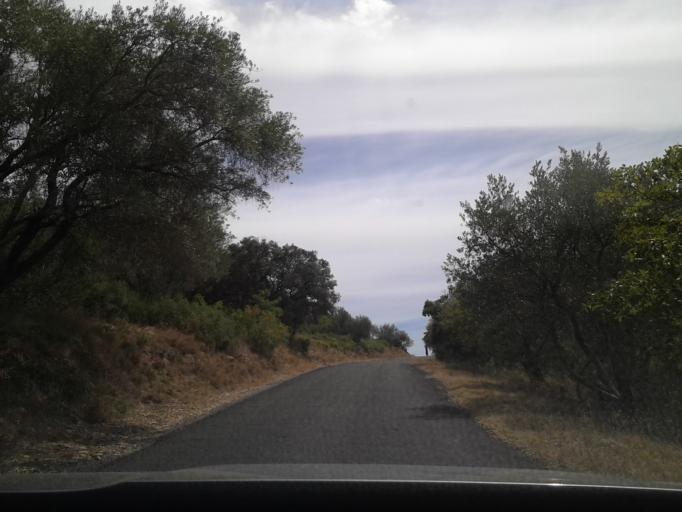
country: FR
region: Languedoc-Roussillon
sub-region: Departement des Pyrenees-Orientales
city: Millas
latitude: 42.7252
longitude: 2.6768
